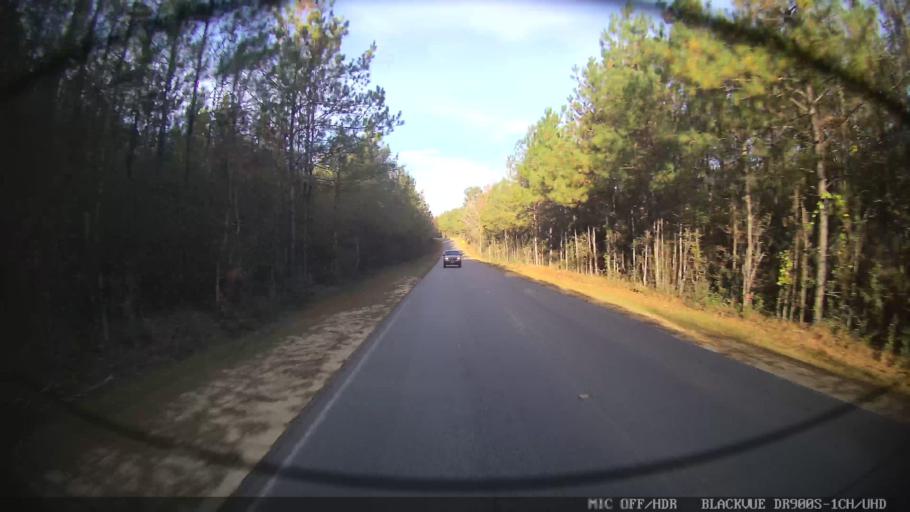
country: US
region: Mississippi
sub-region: Lamar County
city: Purvis
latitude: 31.1502
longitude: -89.3371
